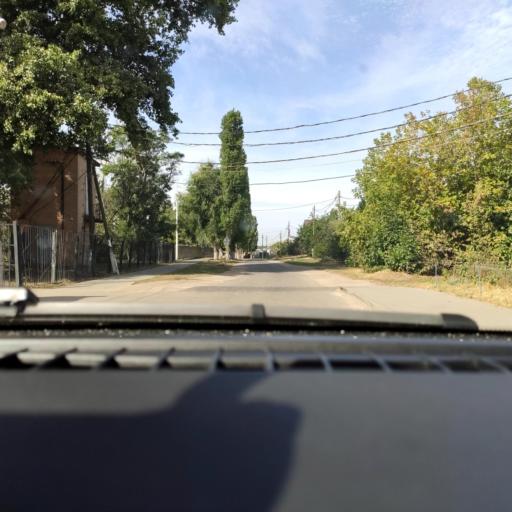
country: RU
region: Voronezj
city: Maslovka
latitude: 51.5514
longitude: 39.2380
